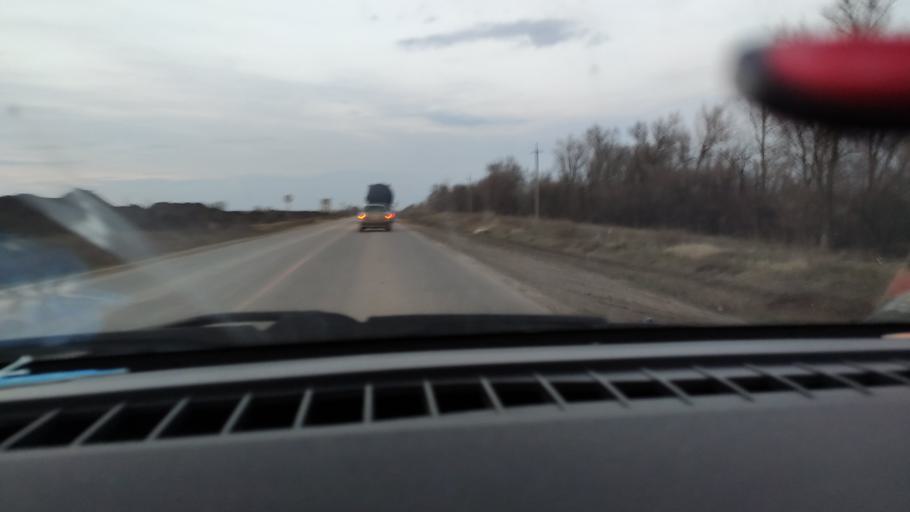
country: RU
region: Saratov
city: Sinodskoye
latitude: 52.0167
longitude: 46.6993
